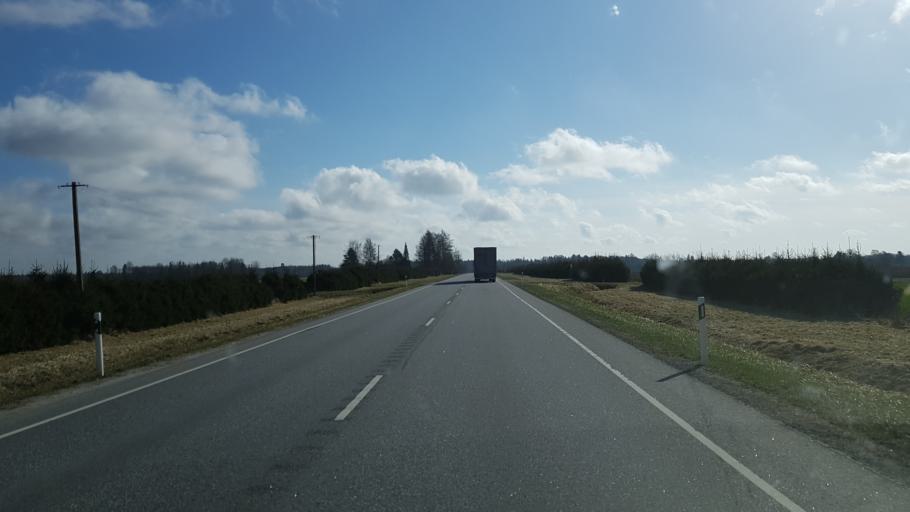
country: EE
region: Paernumaa
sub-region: Vaendra vald (alev)
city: Vandra
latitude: 58.6712
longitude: 25.0976
